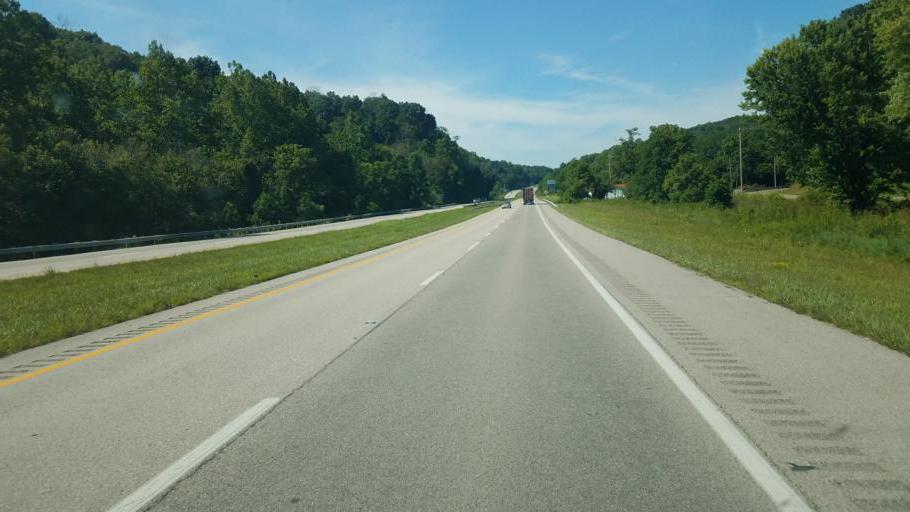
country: US
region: Ohio
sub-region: Meigs County
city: Pomeroy
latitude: 39.0669
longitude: -82.0187
